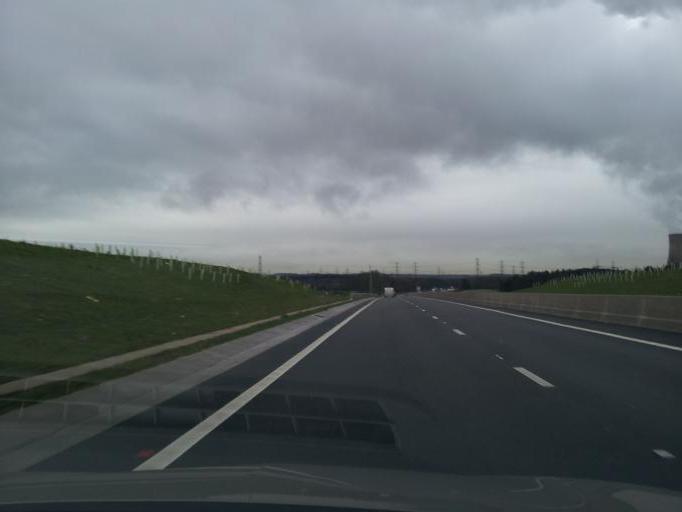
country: GB
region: England
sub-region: Nottinghamshire
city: Gotham
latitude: 52.8669
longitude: -1.2405
